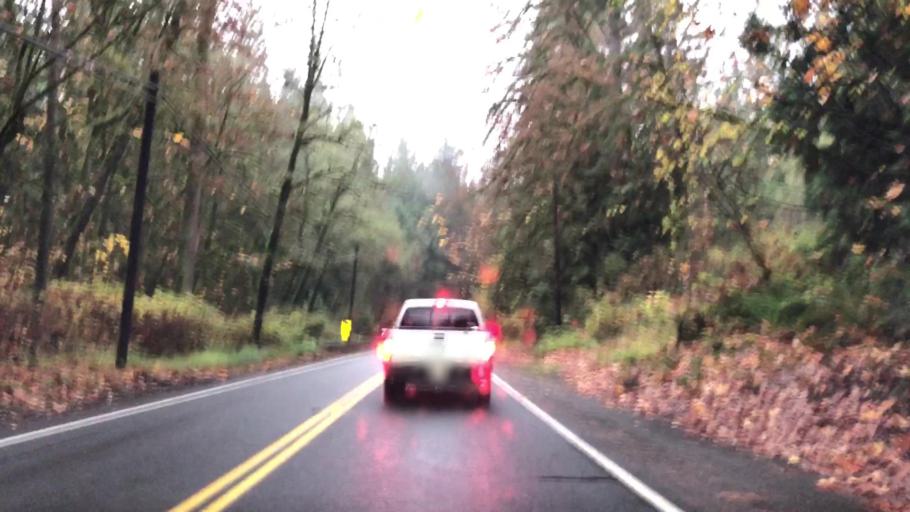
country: US
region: Washington
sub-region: King County
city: Duvall
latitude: 47.7538
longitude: -122.0194
